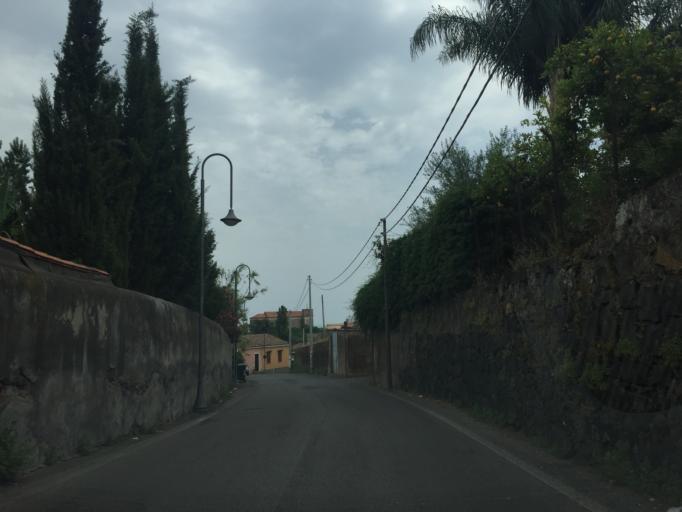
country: IT
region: Sicily
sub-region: Catania
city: Vambolieri
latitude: 37.5778
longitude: 15.1699
